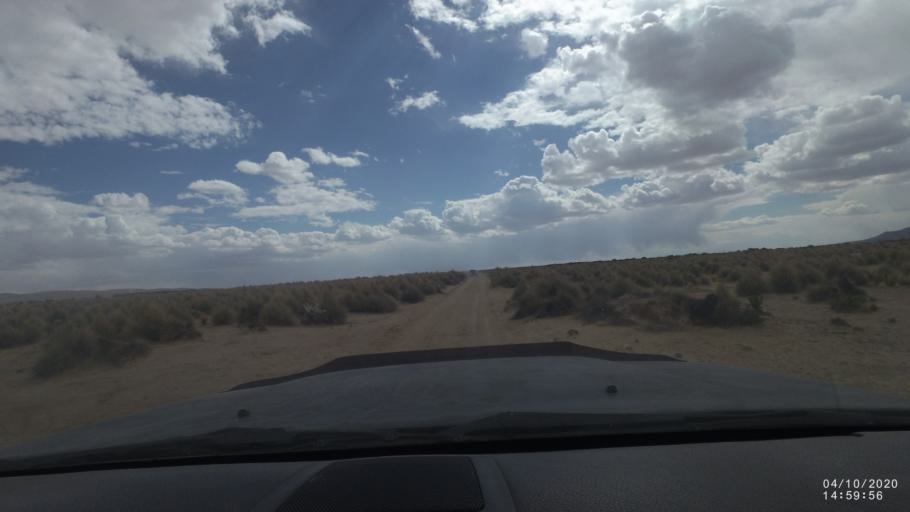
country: BO
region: Oruro
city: Poopo
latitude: -18.6863
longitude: -67.5250
